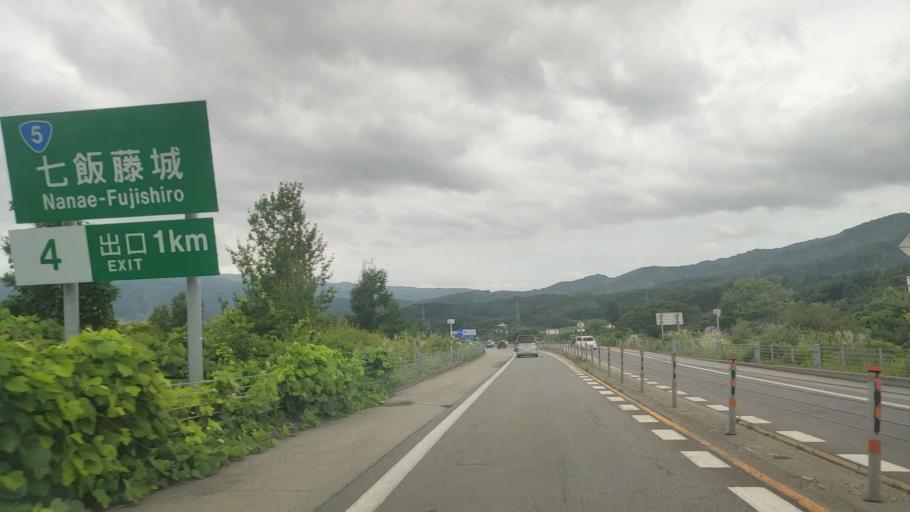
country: JP
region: Hokkaido
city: Nanae
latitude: 41.9184
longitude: 140.6820
